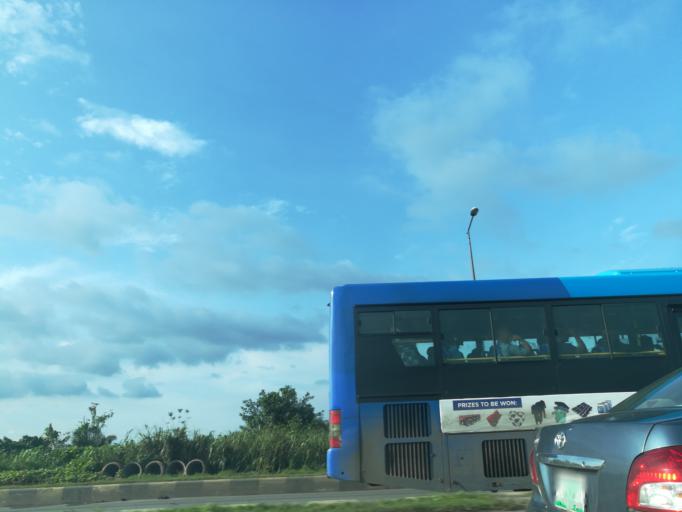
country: NG
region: Lagos
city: Ebute Ikorodu
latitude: 6.6211
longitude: 3.4542
